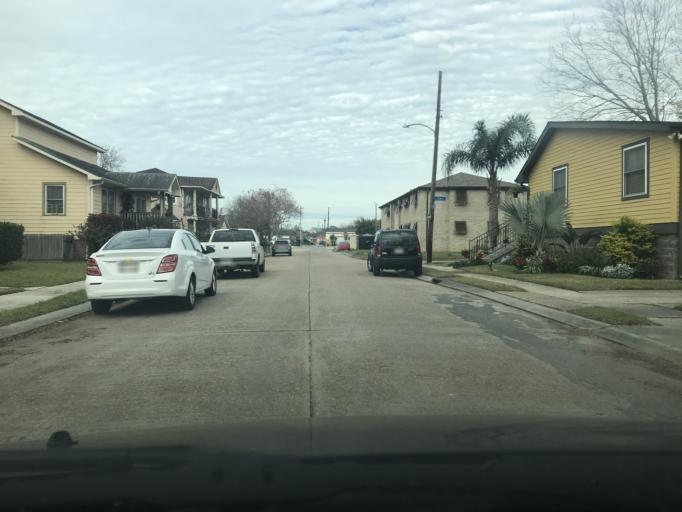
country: US
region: Louisiana
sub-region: Orleans Parish
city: New Orleans
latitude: 29.9565
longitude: -90.1085
